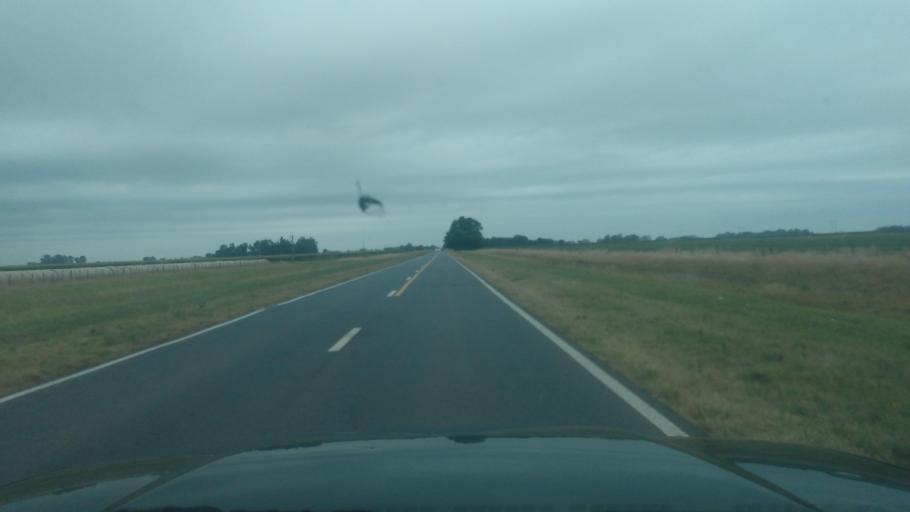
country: AR
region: Buenos Aires
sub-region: Partido de Bragado
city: Bragado
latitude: -35.3062
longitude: -60.6210
